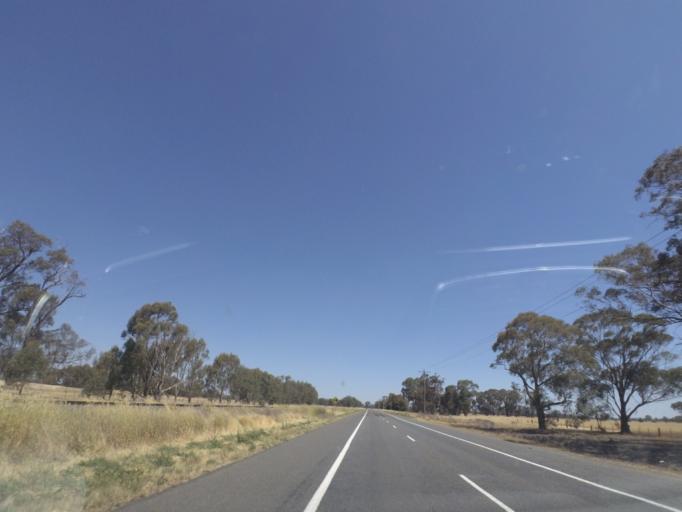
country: AU
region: Victoria
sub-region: Greater Shepparton
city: Shepparton
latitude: -36.2172
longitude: 145.4318
